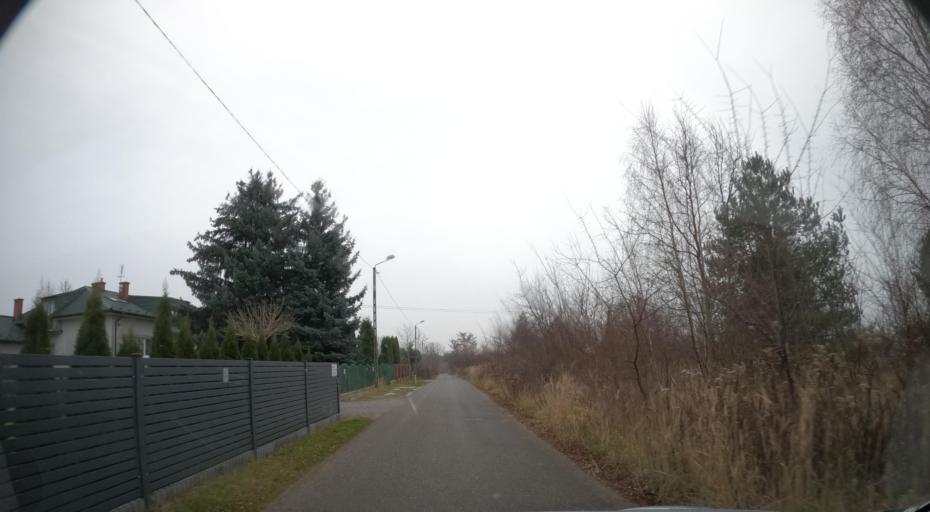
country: PL
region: Masovian Voivodeship
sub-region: Powiat radomski
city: Jastrzebia
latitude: 51.4313
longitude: 21.2300
